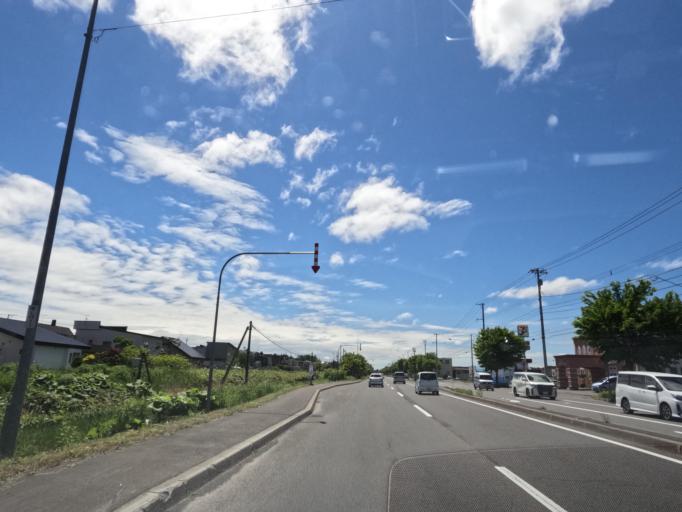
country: JP
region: Hokkaido
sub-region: Asahikawa-shi
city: Asahikawa
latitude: 43.7397
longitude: 142.3605
